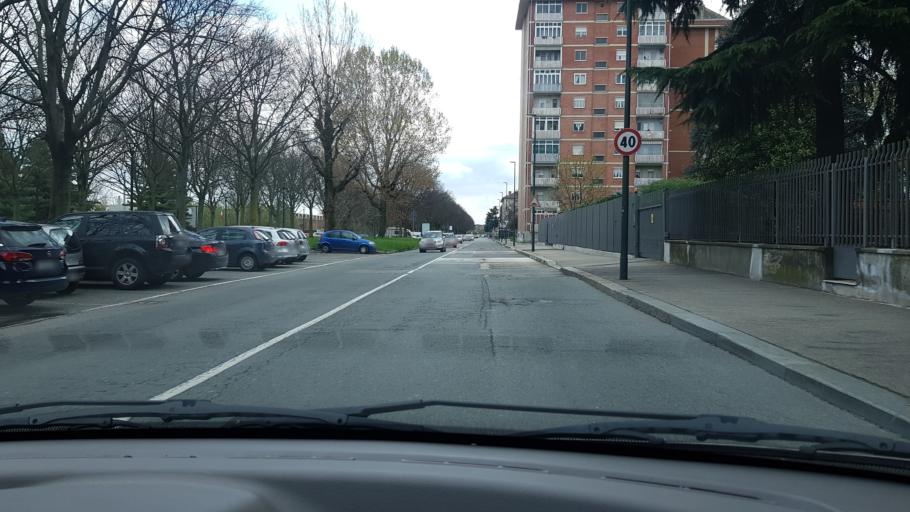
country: IT
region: Piedmont
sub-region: Provincia di Torino
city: Nichelino
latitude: 45.0160
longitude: 7.6381
